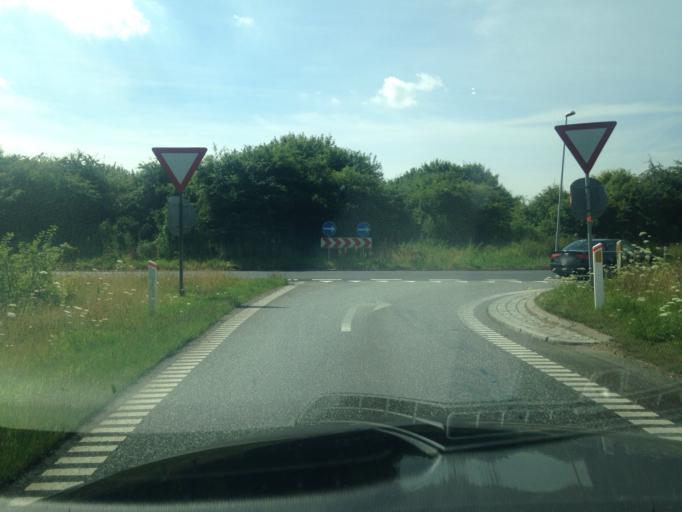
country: DK
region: South Denmark
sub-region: Kolding Kommune
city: Kolding
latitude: 55.5319
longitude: 9.4963
